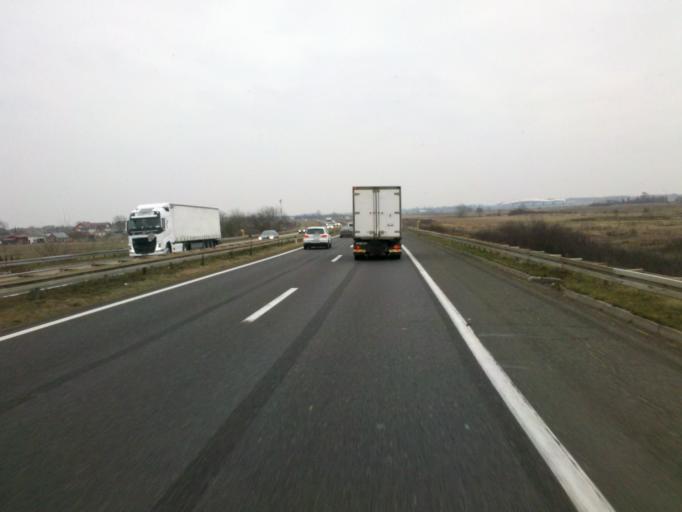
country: HR
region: Zagrebacka
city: Micevec
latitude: 45.7461
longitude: 16.0461
